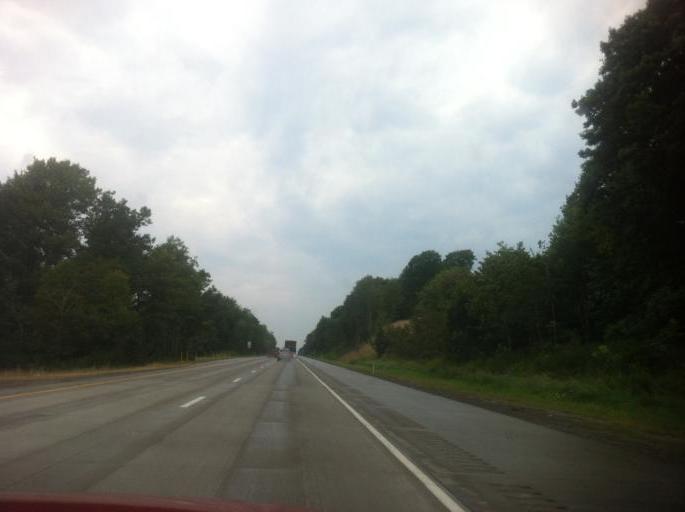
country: US
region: Pennsylvania
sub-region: Jefferson County
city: Falls Creek
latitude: 41.1507
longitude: -78.7998
